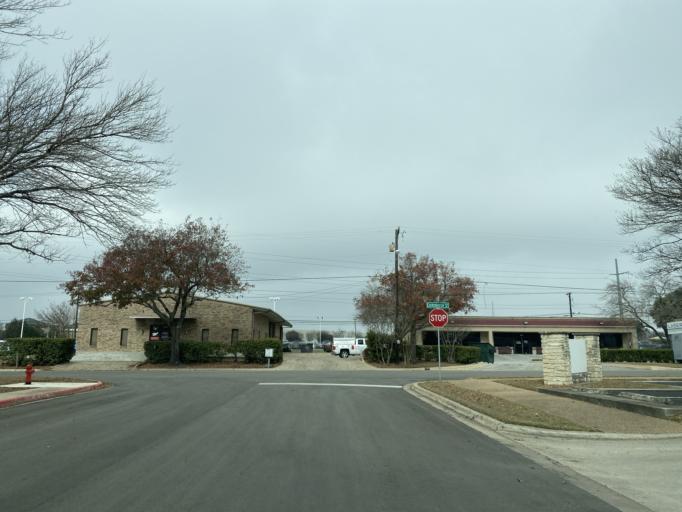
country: US
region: Texas
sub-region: Williamson County
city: Round Rock
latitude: 30.5319
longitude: -97.6857
